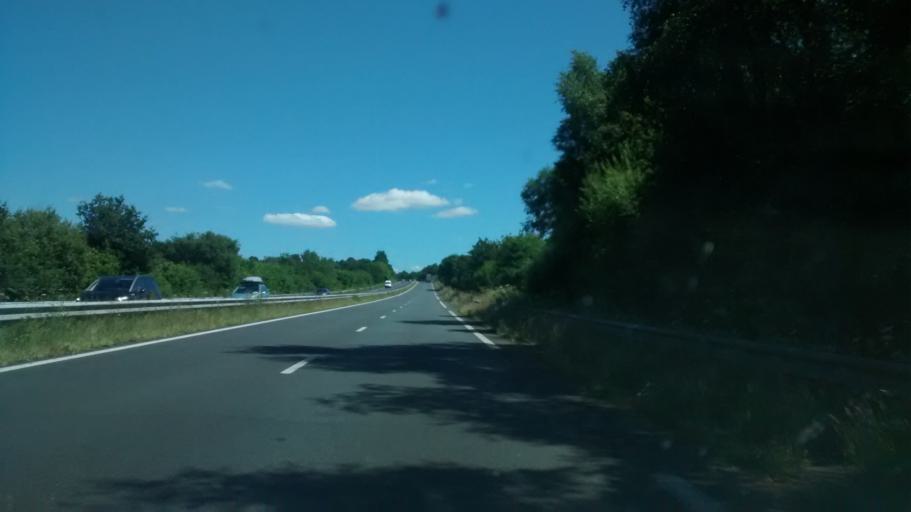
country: FR
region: Brittany
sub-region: Departement des Cotes-d'Armor
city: Plounevez-Moedec
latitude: 48.5550
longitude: -3.4755
